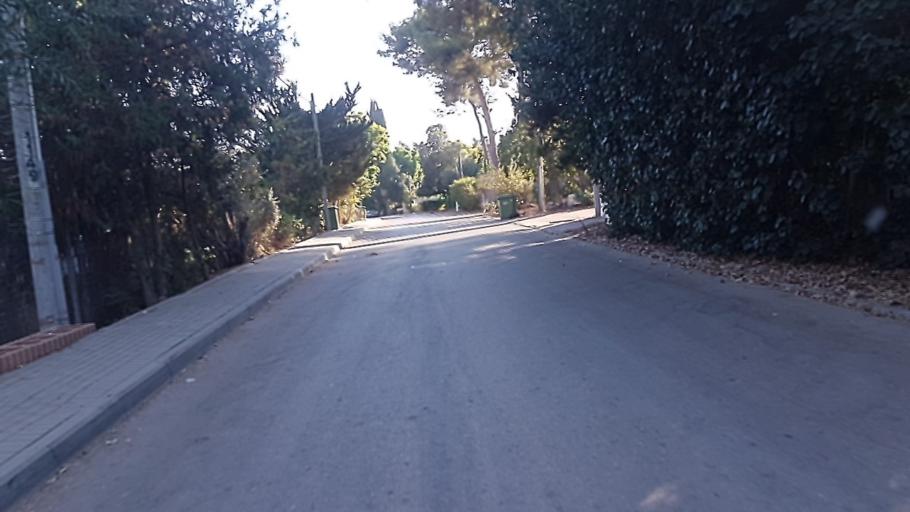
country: IL
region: Central District
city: Hod HaSharon
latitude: 32.1429
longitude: 34.9037
